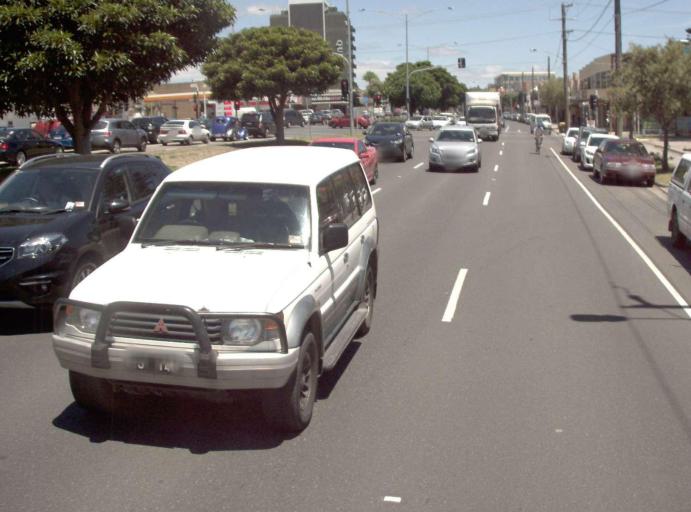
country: AU
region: Victoria
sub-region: Frankston
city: Frankston
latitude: -38.1395
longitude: 145.1227
